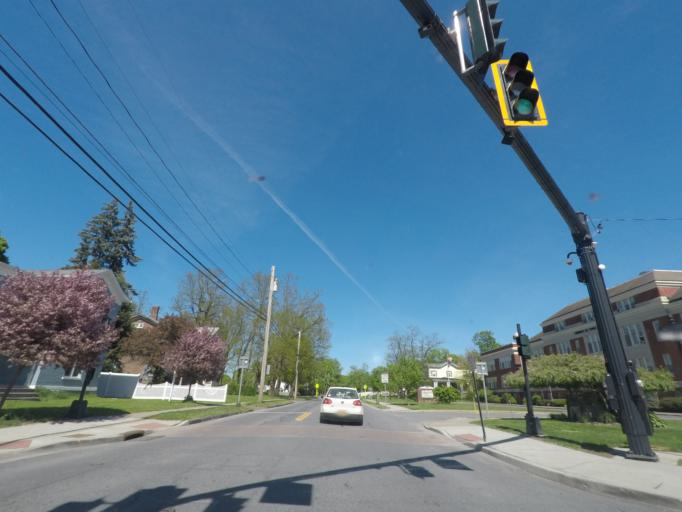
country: US
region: New York
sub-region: Ulster County
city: Saugerties
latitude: 42.0785
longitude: -73.9500
